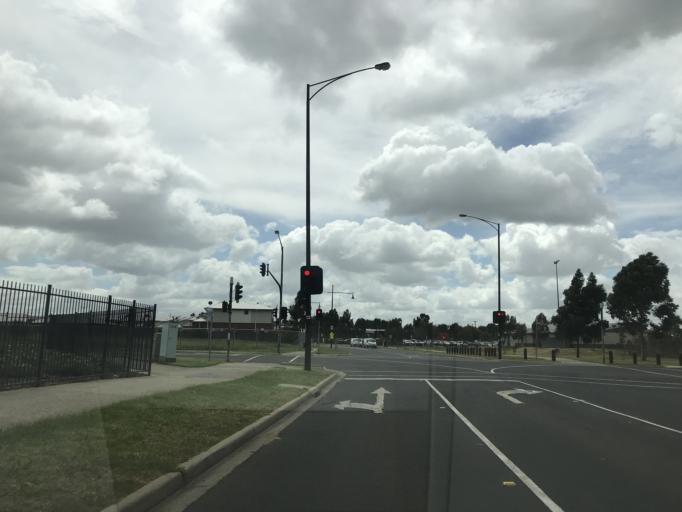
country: AU
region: Victoria
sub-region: Brimbank
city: Derrimut
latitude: -37.7918
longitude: 144.7620
